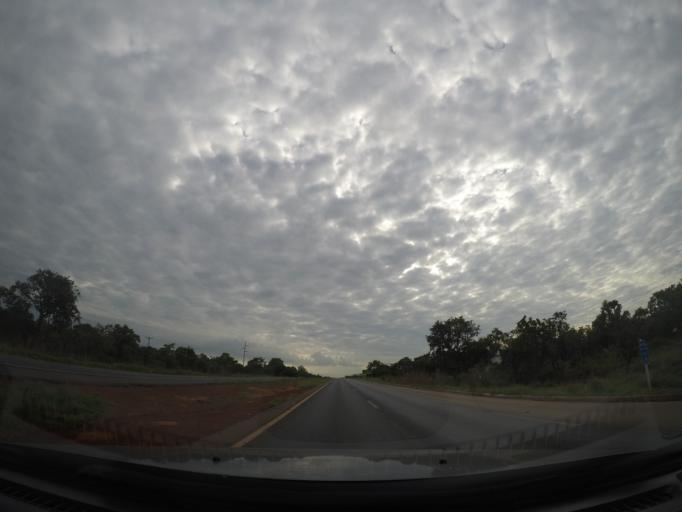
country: BR
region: Goias
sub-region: Planaltina
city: Planaltina
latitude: -15.5964
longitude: -47.6405
